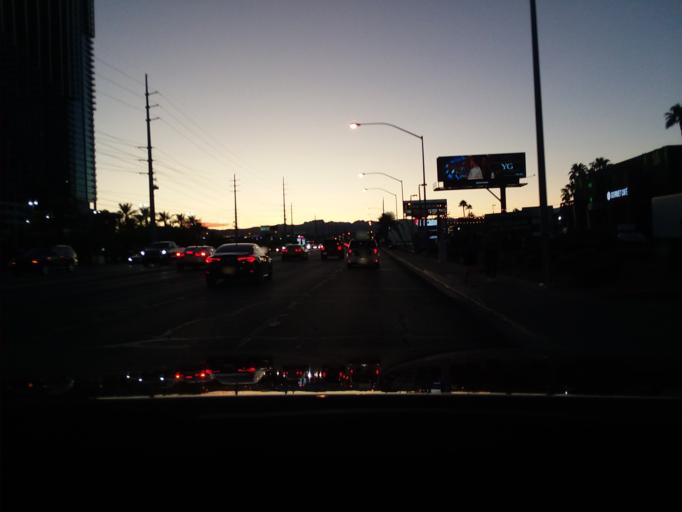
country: US
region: Nevada
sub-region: Clark County
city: Spring Valley
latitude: 36.1156
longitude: -115.1958
